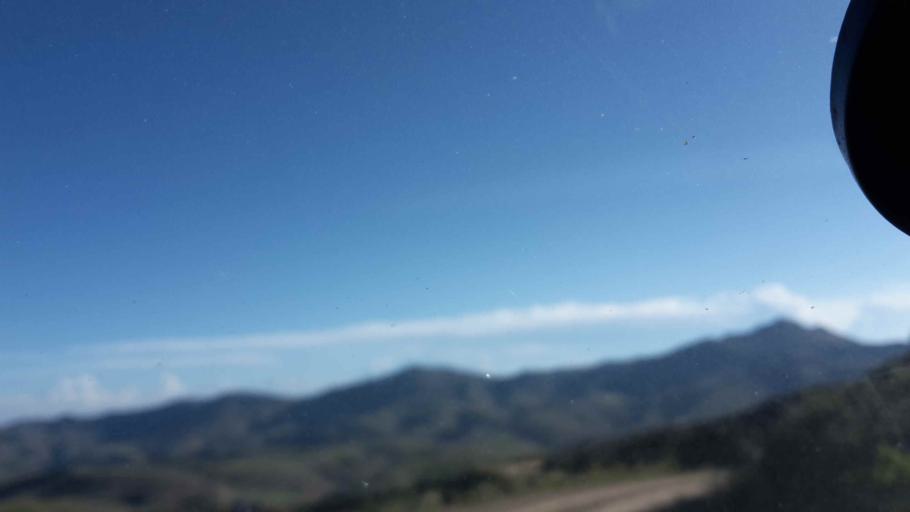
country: BO
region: Cochabamba
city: Arani
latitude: -17.7352
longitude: -65.6216
